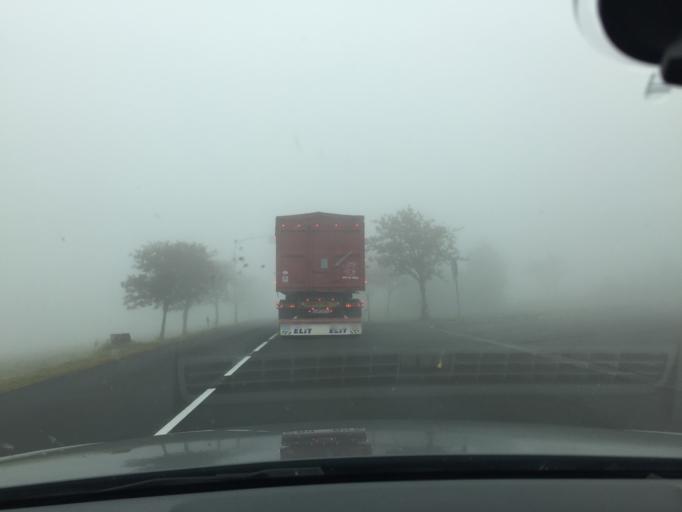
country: CZ
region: Ustecky
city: Libouchec
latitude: 50.7734
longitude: 13.9780
